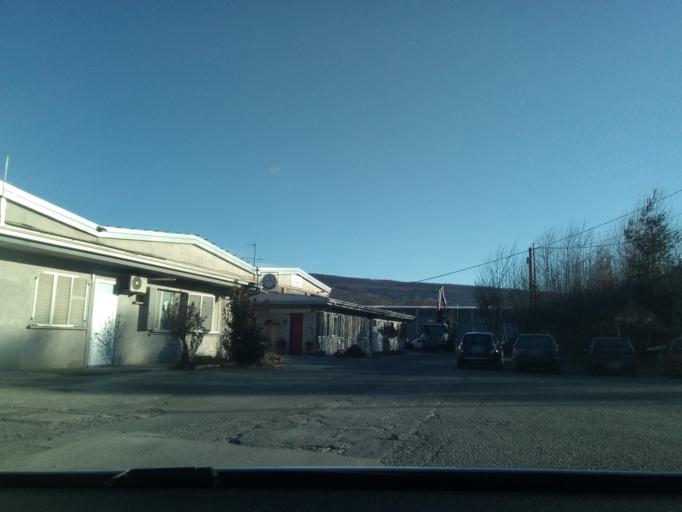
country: IT
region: Piedmont
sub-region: Provincia di Torino
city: Cascinette d'Ivrea
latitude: 45.4713
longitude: 7.9088
